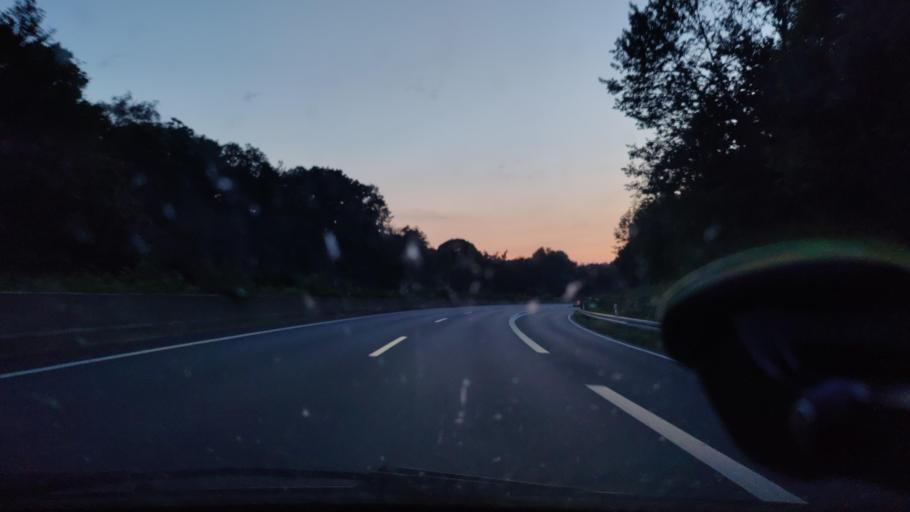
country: DE
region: North Rhine-Westphalia
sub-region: Regierungsbezirk Arnsberg
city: Bochum
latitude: 51.4537
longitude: 7.2170
